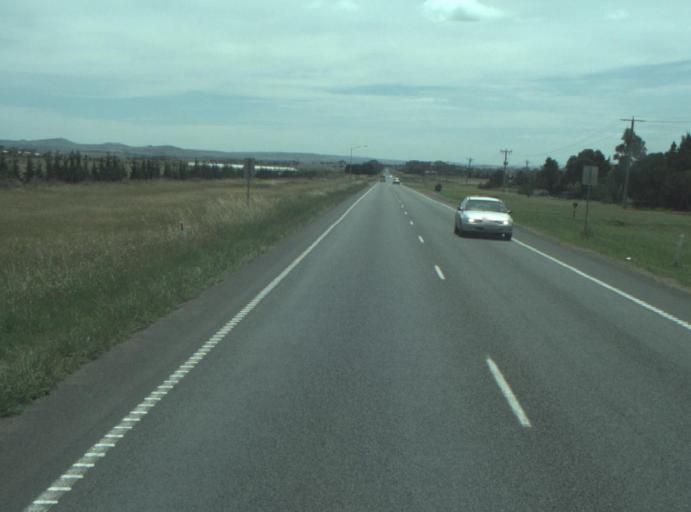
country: AU
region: Victoria
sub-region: Greater Geelong
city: Lara
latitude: -38.0209
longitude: 144.3526
